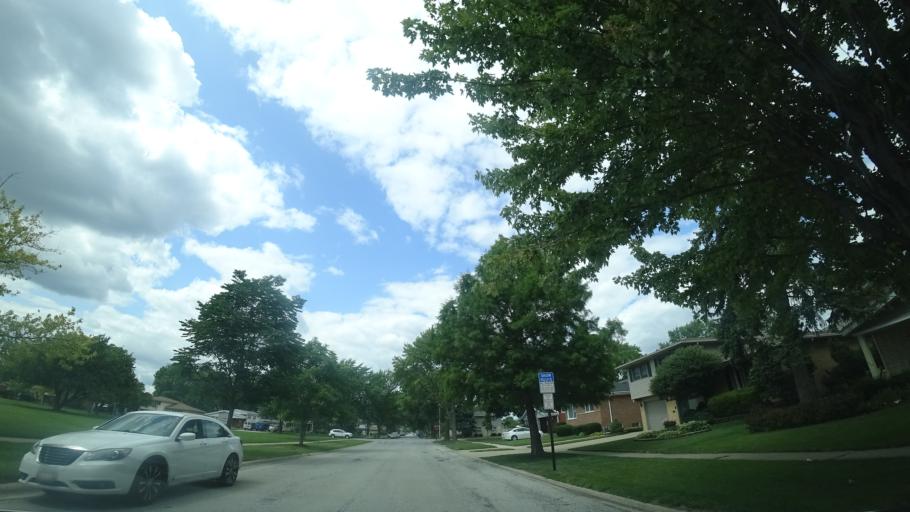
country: US
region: Illinois
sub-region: Cook County
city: Oak Lawn
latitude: 41.6976
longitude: -87.7351
